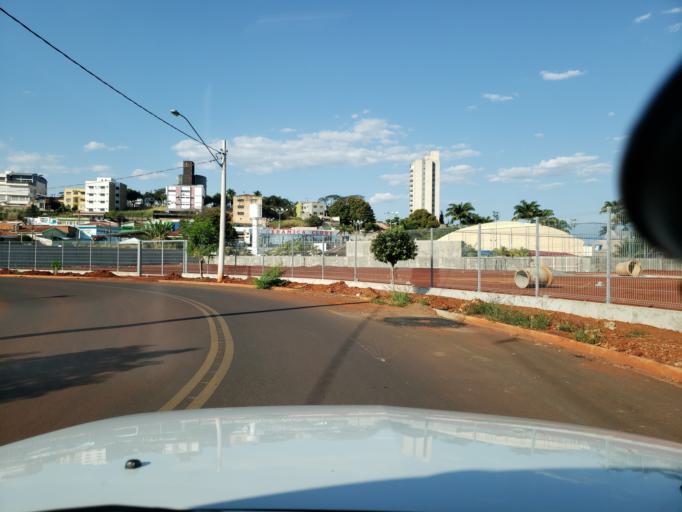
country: BR
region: Sao Paulo
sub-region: Moji-Guacu
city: Mogi-Gaucu
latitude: -22.3700
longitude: -46.9472
